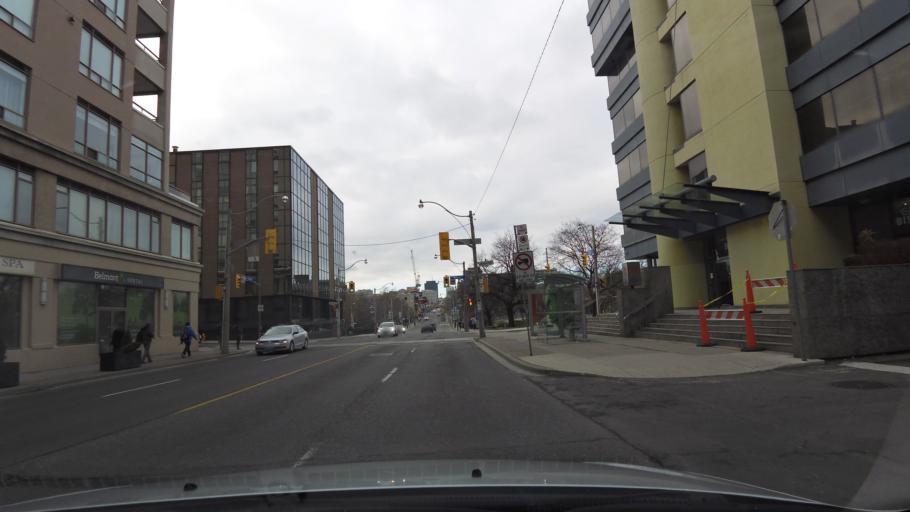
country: CA
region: Ontario
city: Toronto
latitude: 43.6753
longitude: -79.3888
